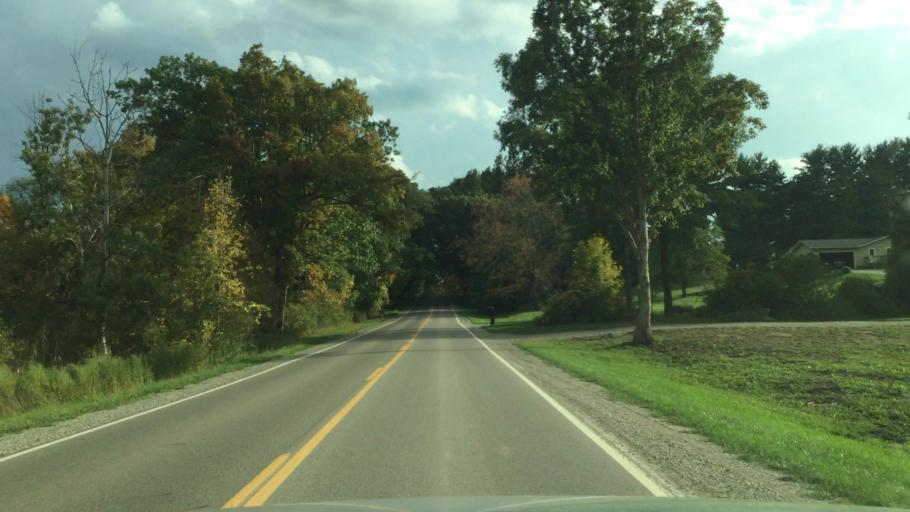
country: US
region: Michigan
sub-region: Genesee County
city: Fenton
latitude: 42.6776
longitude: -83.7021
